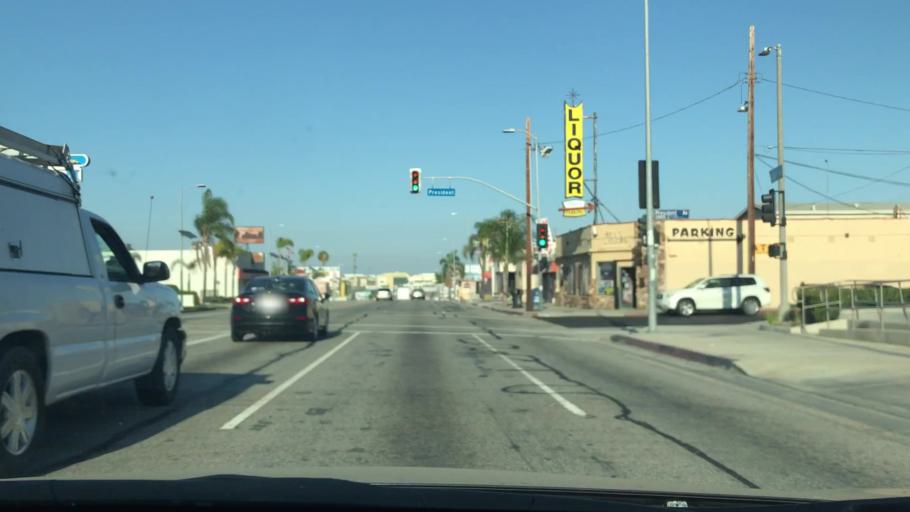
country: US
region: California
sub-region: Los Angeles County
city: Lomita
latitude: 33.7894
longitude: -118.3046
